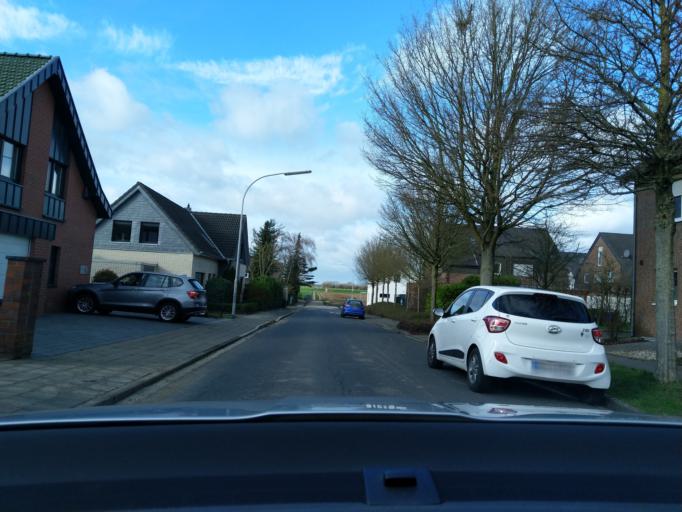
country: DE
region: North Rhine-Westphalia
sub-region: Regierungsbezirk Dusseldorf
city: Monchengladbach
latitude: 51.1320
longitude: 6.4033
